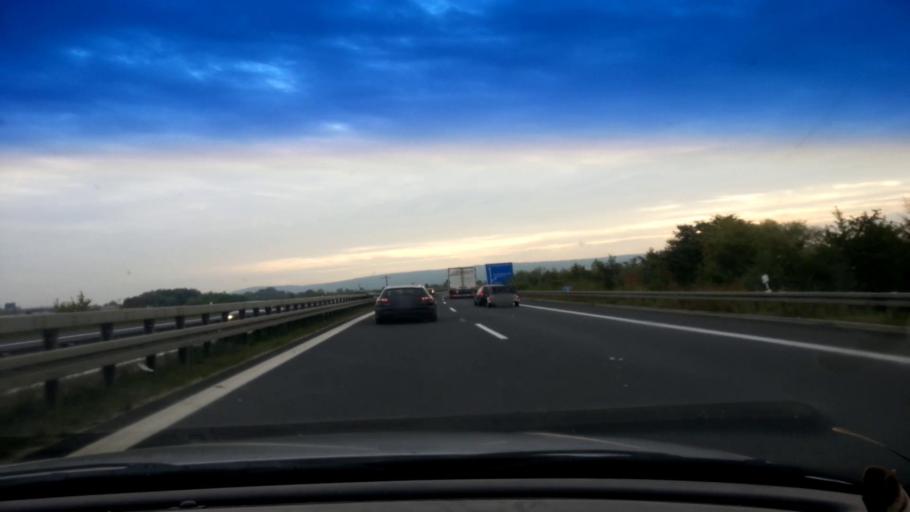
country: DE
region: Bavaria
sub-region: Upper Franconia
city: Breitengussbach
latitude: 49.9821
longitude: 10.8914
